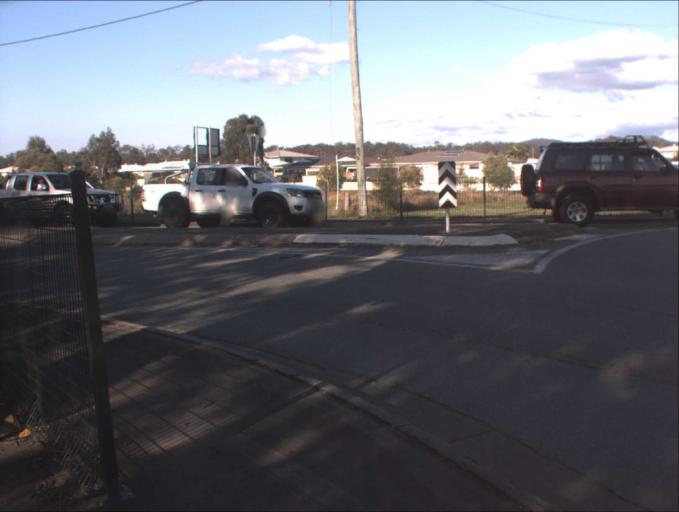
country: AU
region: Queensland
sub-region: Logan
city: Chambers Flat
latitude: -27.7658
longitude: 153.1091
